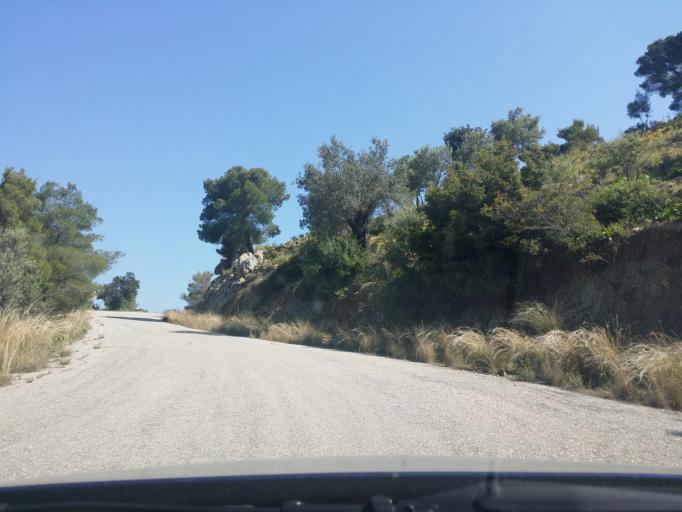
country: GR
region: Attica
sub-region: Nomos Piraios
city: Poros
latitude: 37.5221
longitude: 23.4831
